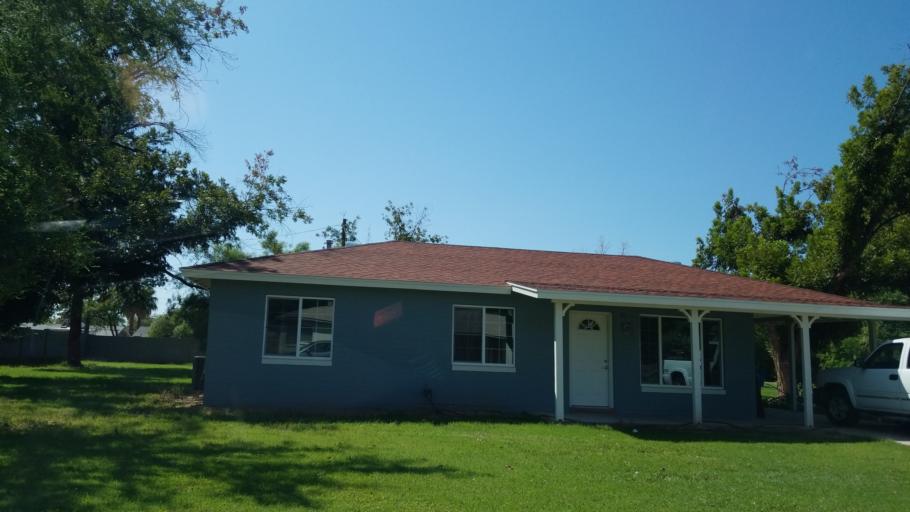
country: US
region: Arizona
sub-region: Maricopa County
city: Glendale
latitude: 33.5575
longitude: -112.0972
